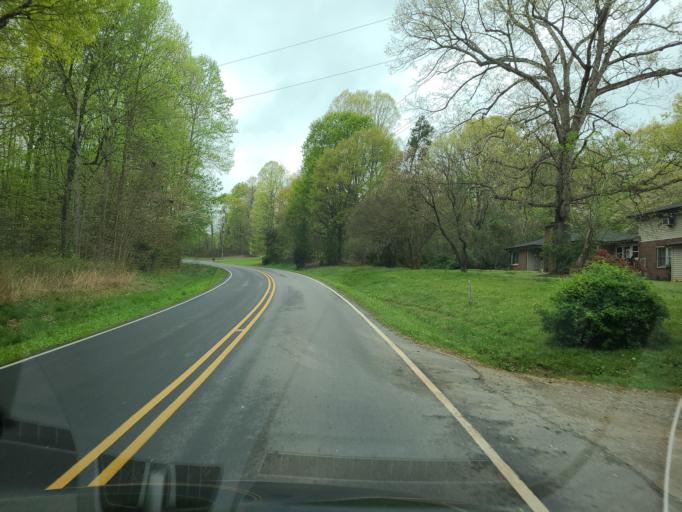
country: US
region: North Carolina
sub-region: Gaston County
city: Cherryville
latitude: 35.4549
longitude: -81.3513
